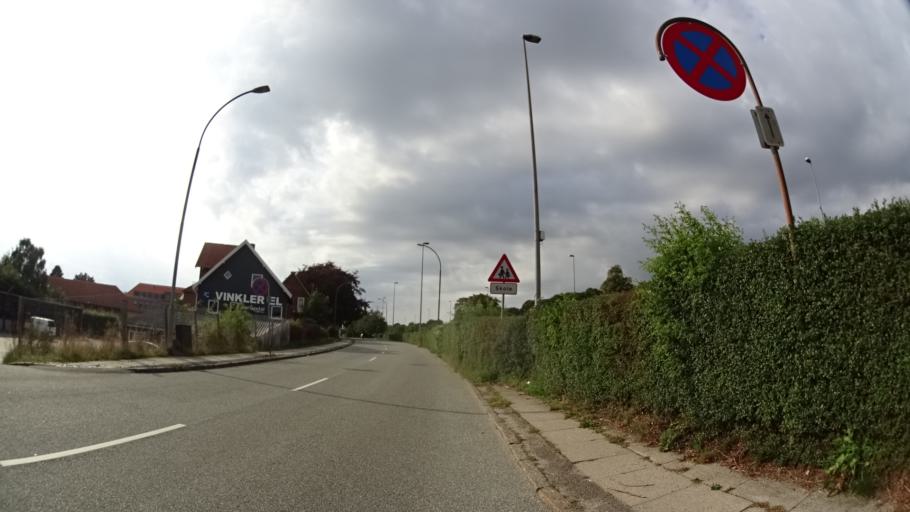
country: DK
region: Central Jutland
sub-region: Arhus Kommune
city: Stavtrup
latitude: 56.1531
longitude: 10.1117
